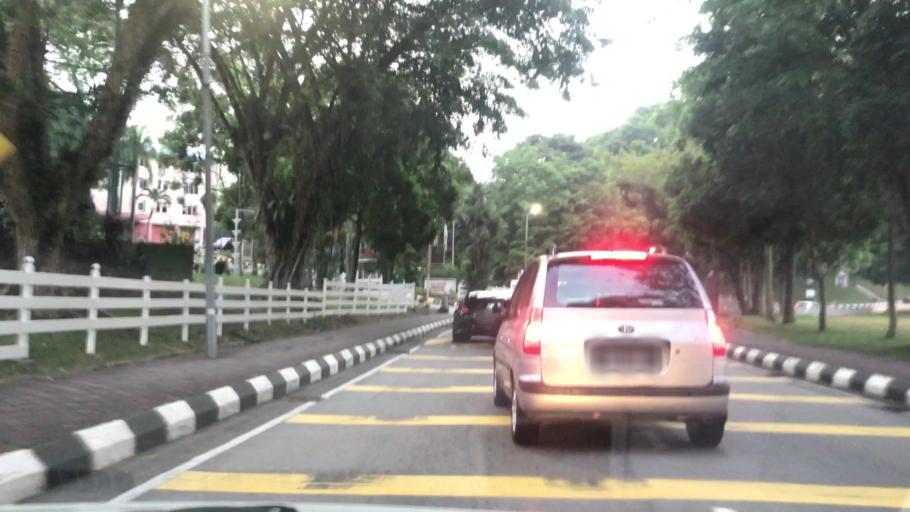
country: MY
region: Kuala Lumpur
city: Kuala Lumpur
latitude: 3.1184
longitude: 101.6600
